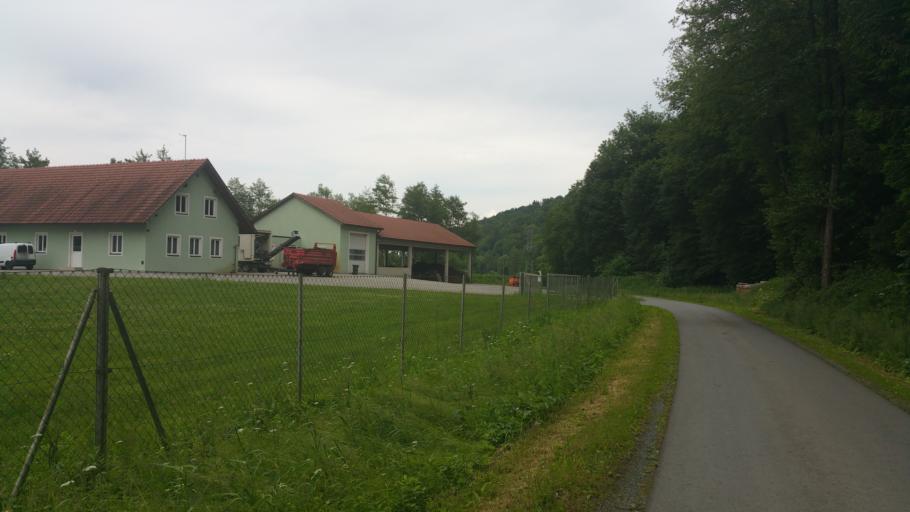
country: AT
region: Styria
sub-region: Politischer Bezirk Leibnitz
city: Gleinstatten
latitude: 46.7343
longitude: 15.3362
